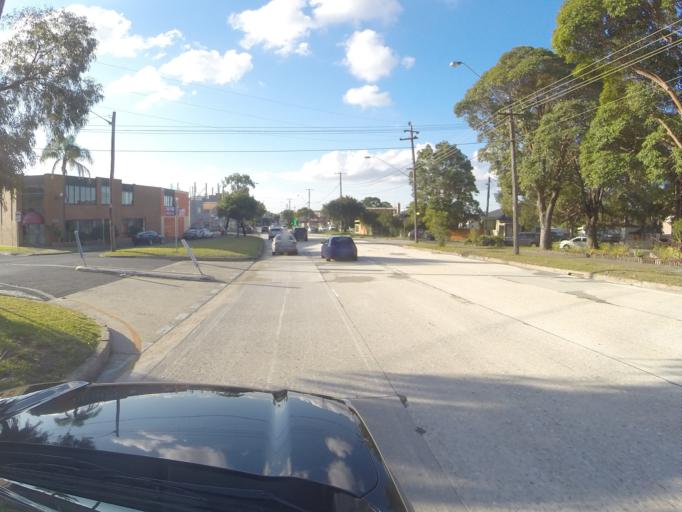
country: AU
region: New South Wales
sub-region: Rockdale
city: Bexley
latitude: -33.9592
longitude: 151.1175
